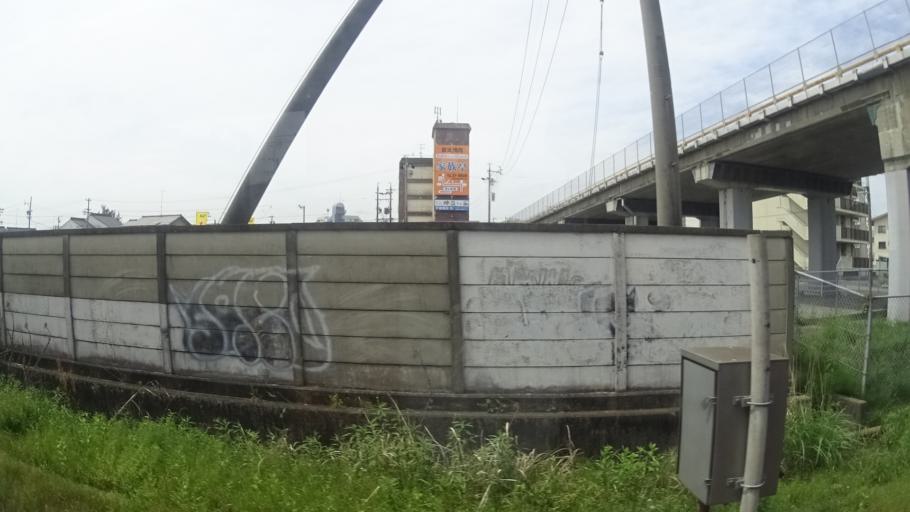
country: JP
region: Mie
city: Hisai-motomachi
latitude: 34.5731
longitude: 136.5392
